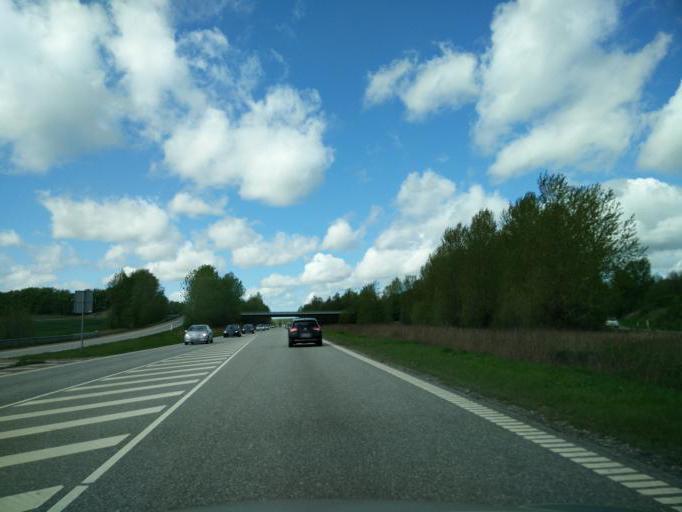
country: DK
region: Capital Region
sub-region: Allerod Kommune
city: Lillerod
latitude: 55.8620
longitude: 12.3188
